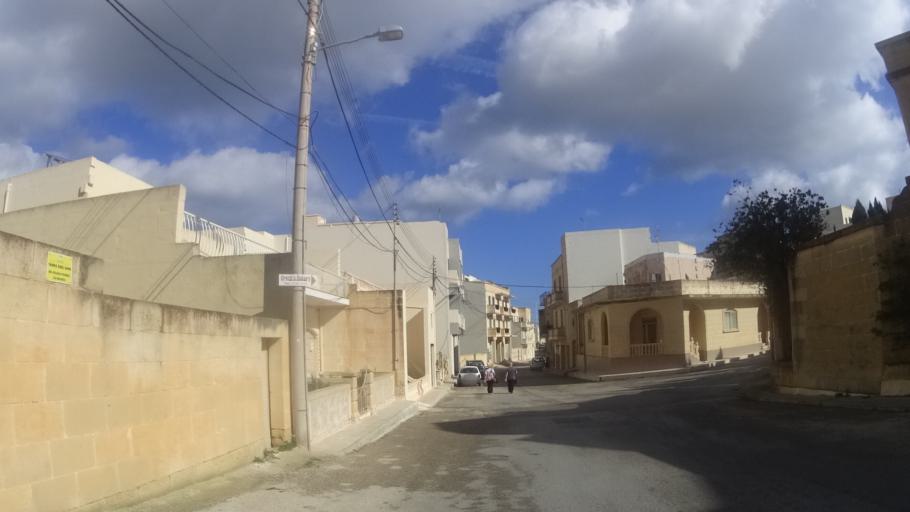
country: MT
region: In-Nadur
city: Nadur
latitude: 36.0372
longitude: 14.2868
